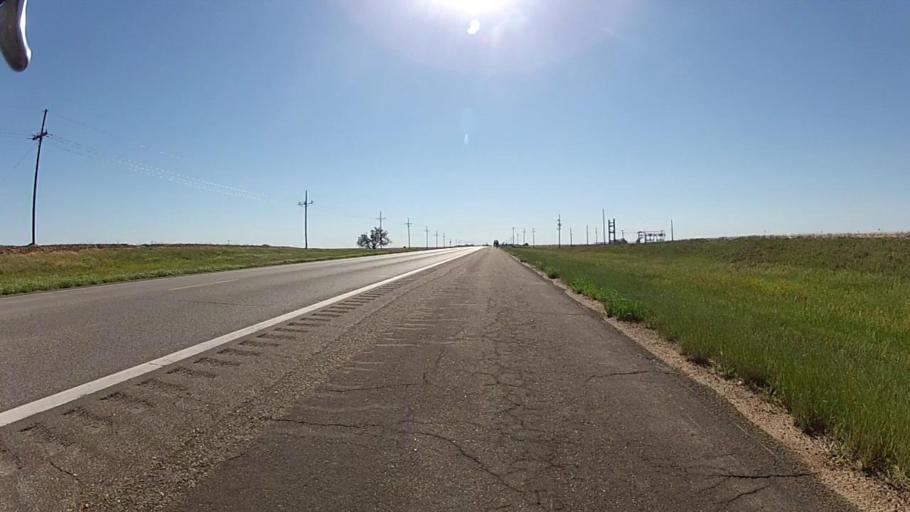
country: US
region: Kansas
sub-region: Kiowa County
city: Greensburg
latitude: 37.5862
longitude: -99.6151
